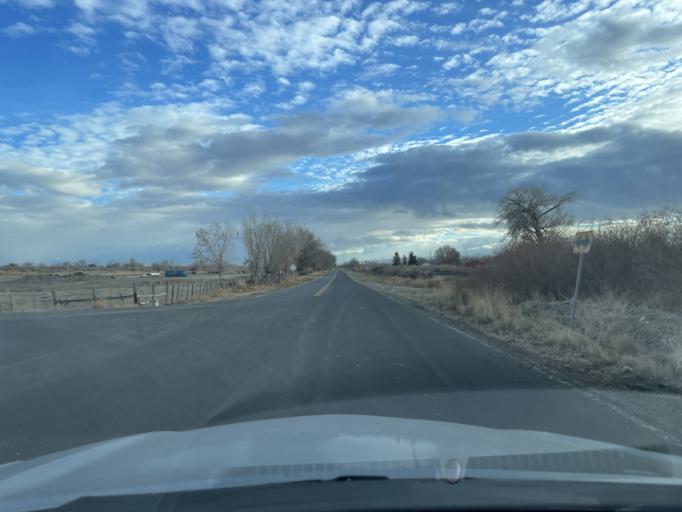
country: US
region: Colorado
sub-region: Montrose County
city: Olathe
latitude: 38.6352
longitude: -107.9911
